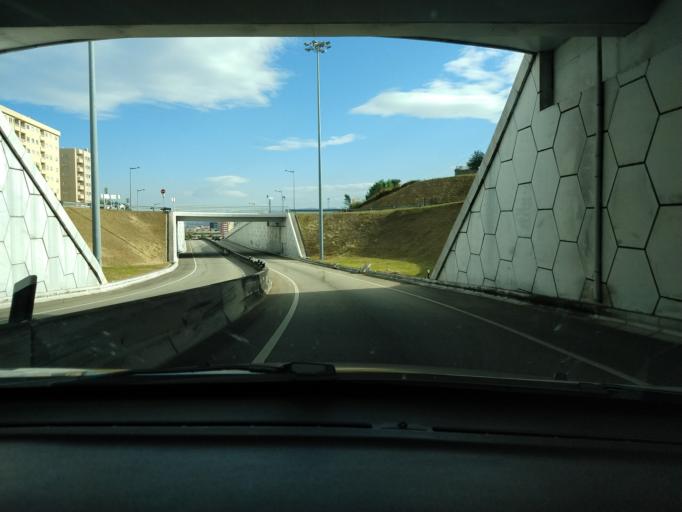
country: PT
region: Porto
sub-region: Vila Nova de Gaia
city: Vilar de Andorinho
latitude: 41.1201
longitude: -8.6012
